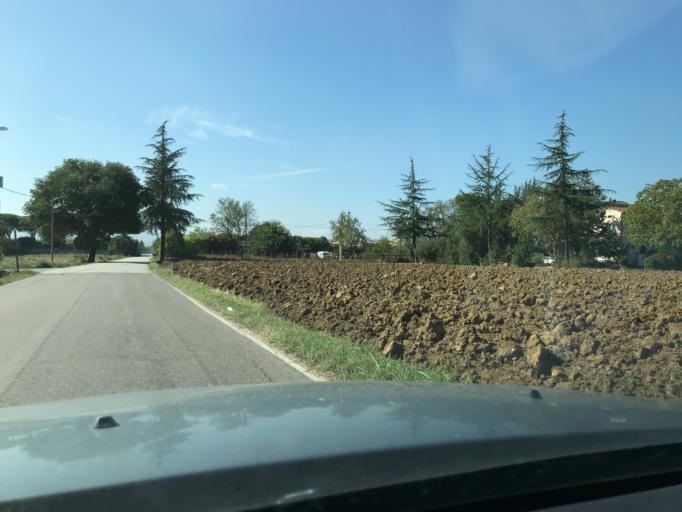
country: IT
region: Umbria
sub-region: Provincia di Perugia
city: Ospedalicchio
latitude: 43.0852
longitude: 12.5074
